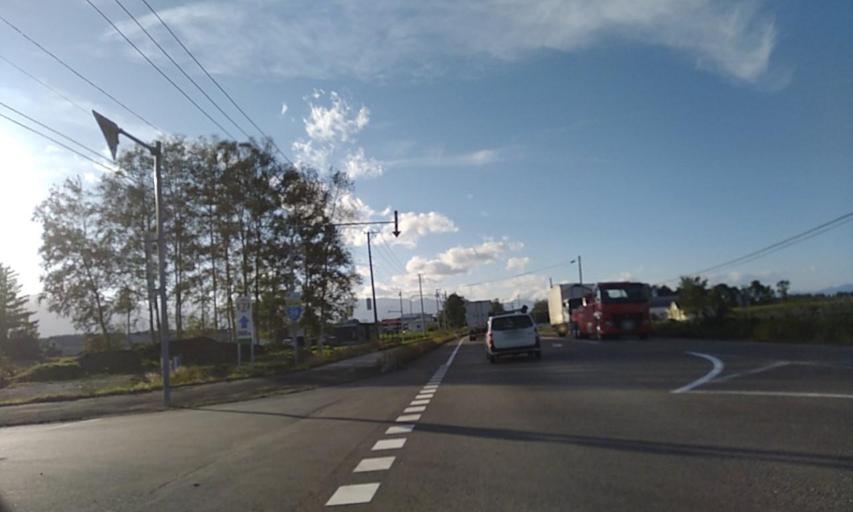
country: JP
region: Hokkaido
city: Otofuke
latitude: 42.9425
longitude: 142.9504
